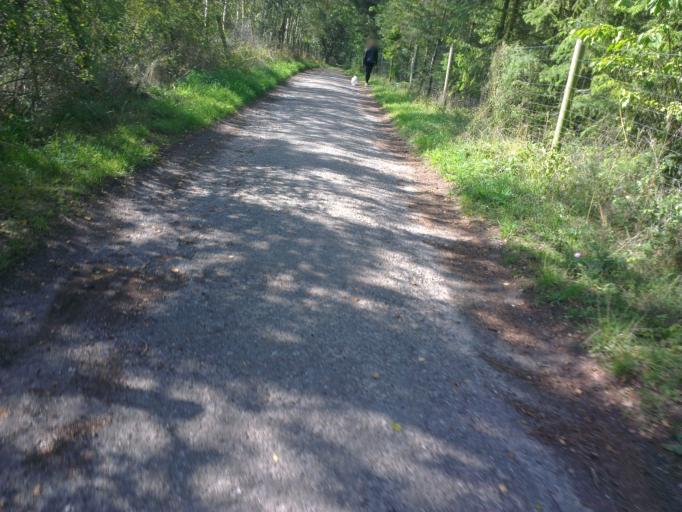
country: DK
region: Capital Region
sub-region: Frederikssund Kommune
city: Skibby
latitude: 55.7421
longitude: 11.9816
